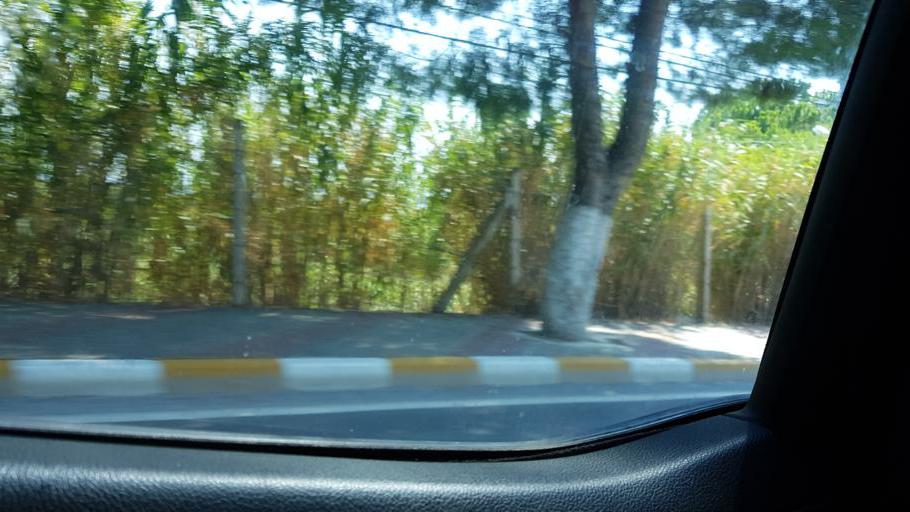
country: TR
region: Izmir
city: Urla
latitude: 38.3571
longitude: 26.7714
